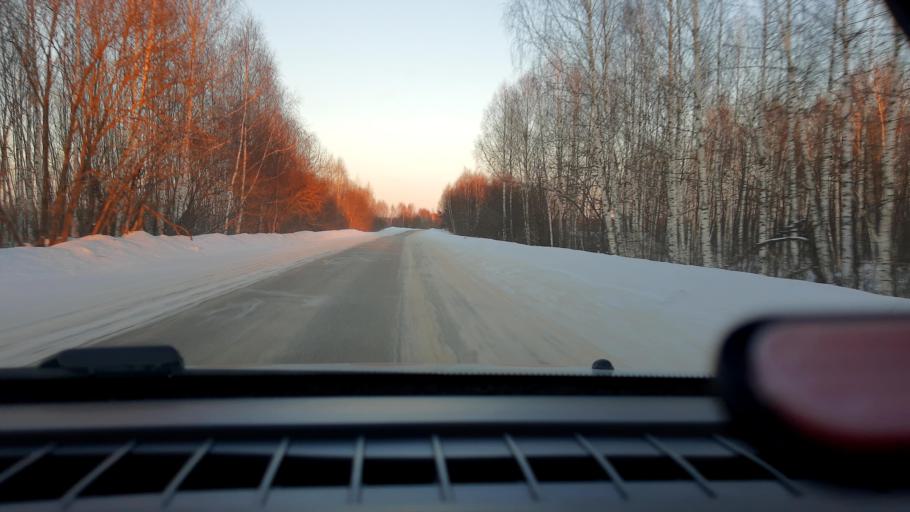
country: RU
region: Nizjnij Novgorod
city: Lyskovo
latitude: 56.1351
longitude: 45.0314
